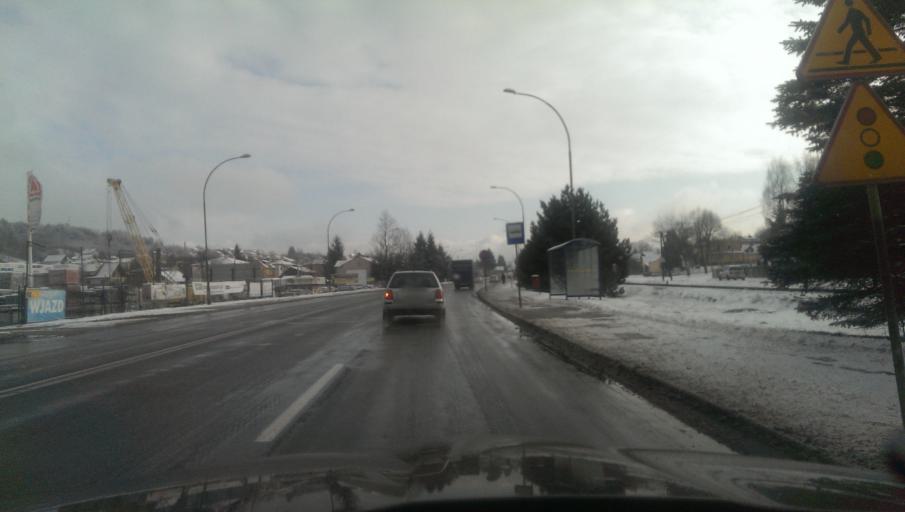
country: PL
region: Subcarpathian Voivodeship
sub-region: Powiat sanocki
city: Sanok
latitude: 49.5691
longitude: 22.1648
